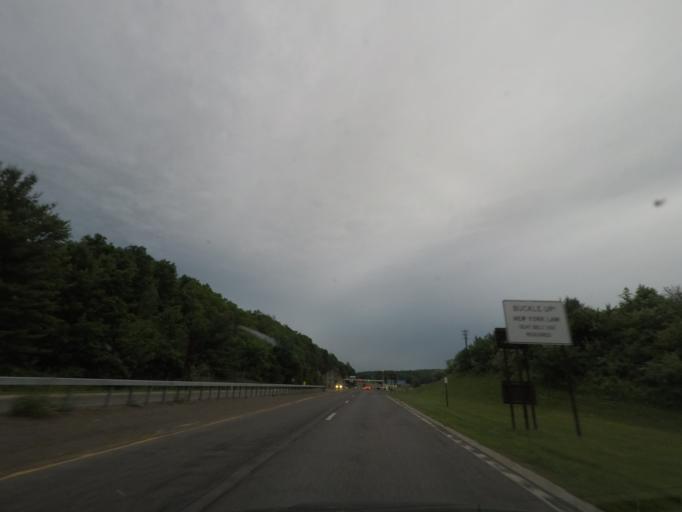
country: US
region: New York
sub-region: Columbia County
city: Chatham
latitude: 42.4156
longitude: -73.5487
